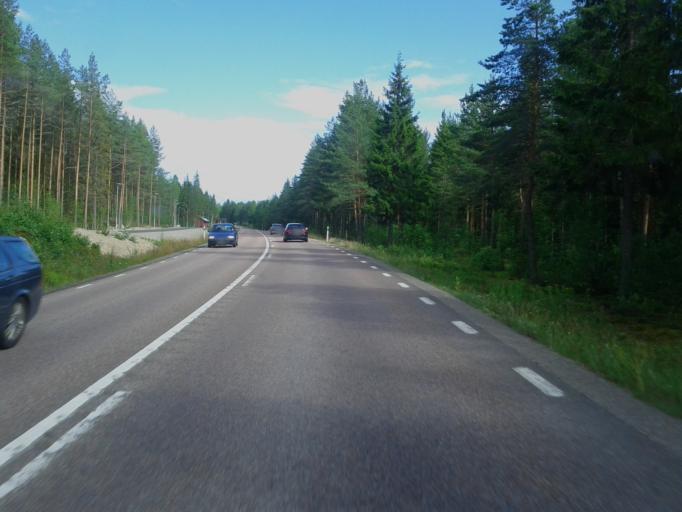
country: SE
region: Dalarna
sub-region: Faluns Kommun
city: Grycksbo
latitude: 60.6718
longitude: 15.5170
